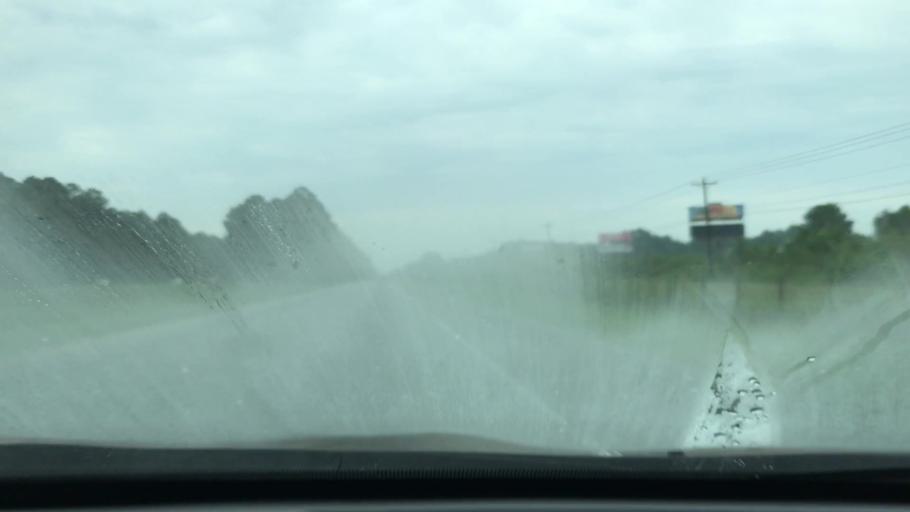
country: US
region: South Carolina
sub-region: Jasper County
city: Ridgeland
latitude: 32.5285
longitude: -80.9593
